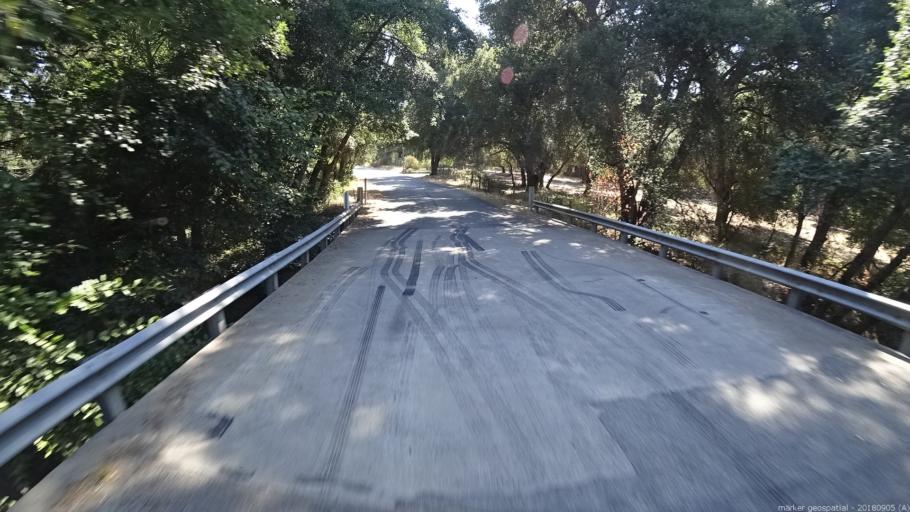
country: US
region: California
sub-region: Monterey County
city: Carmel Valley Village
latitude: 36.3965
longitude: -121.6494
